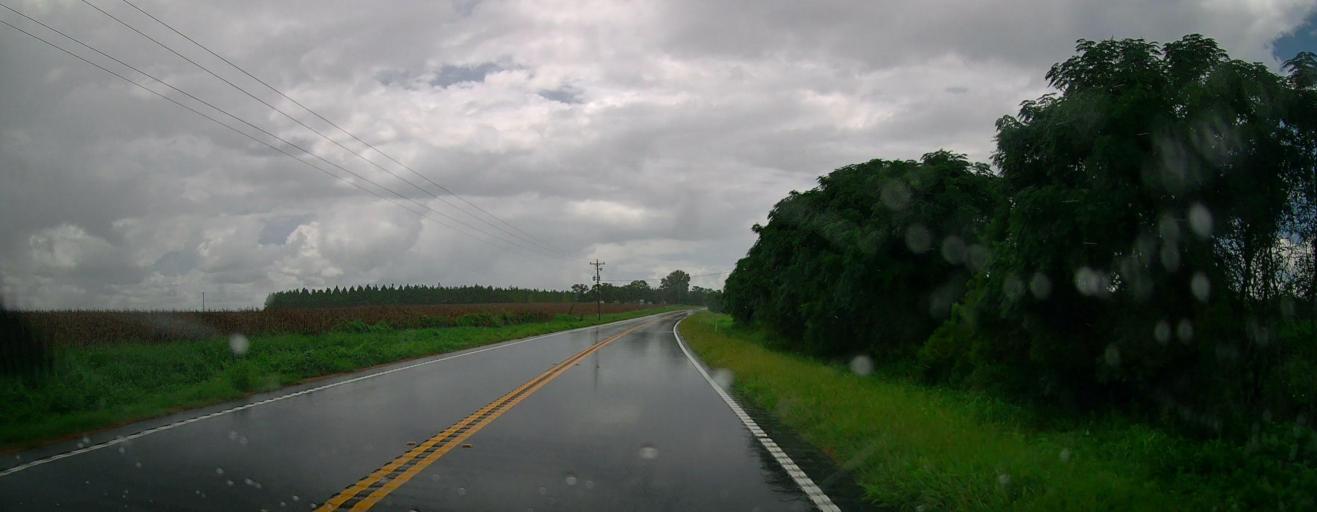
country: US
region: Georgia
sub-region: Pulaski County
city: Hawkinsville
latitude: 32.1946
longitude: -83.5171
